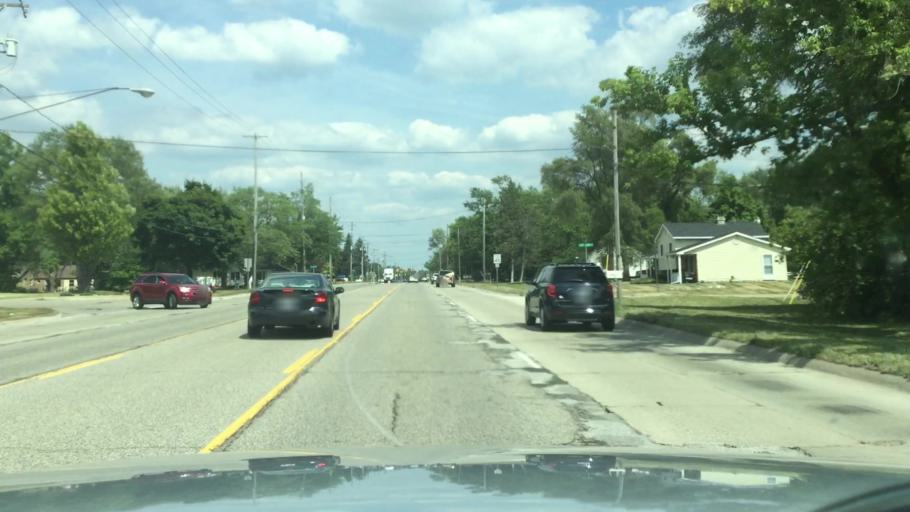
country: US
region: Michigan
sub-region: Genesee County
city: Grand Blanc
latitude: 42.9445
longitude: -83.6580
